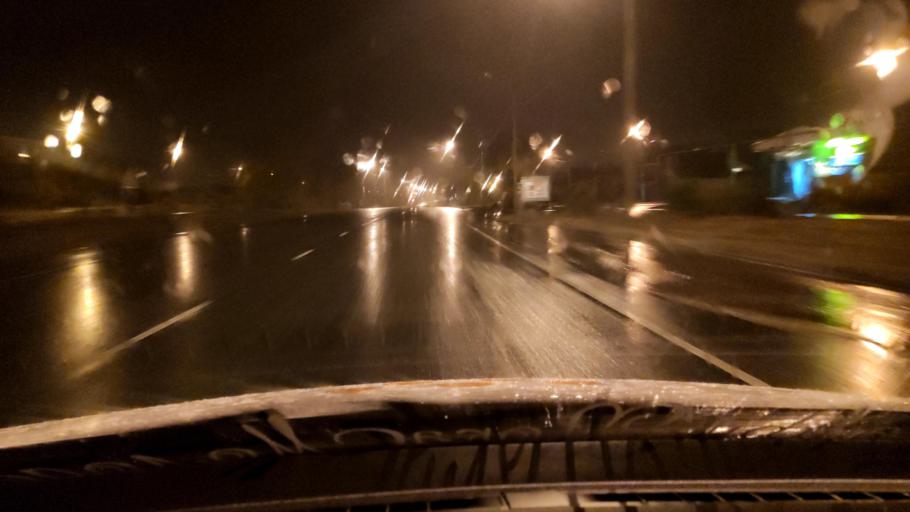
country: RU
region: Voronezj
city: Pridonskoy
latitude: 51.7029
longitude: 39.0769
